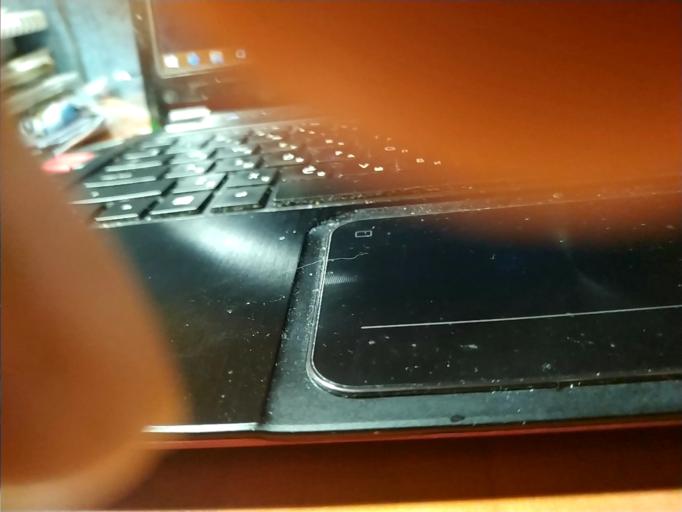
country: RU
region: Tverskaya
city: Ves'yegonsk
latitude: 58.7024
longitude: 37.5439
